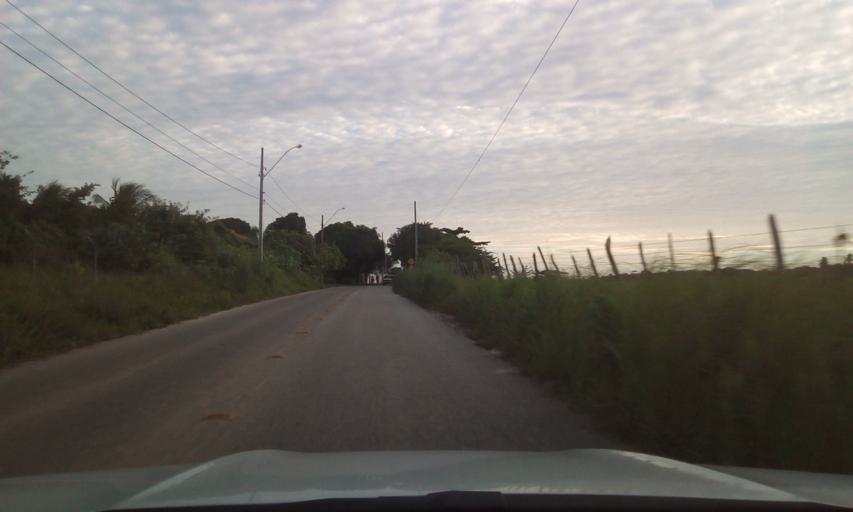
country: BR
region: Paraiba
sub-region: Conde
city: Conde
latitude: -7.2237
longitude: -34.8154
